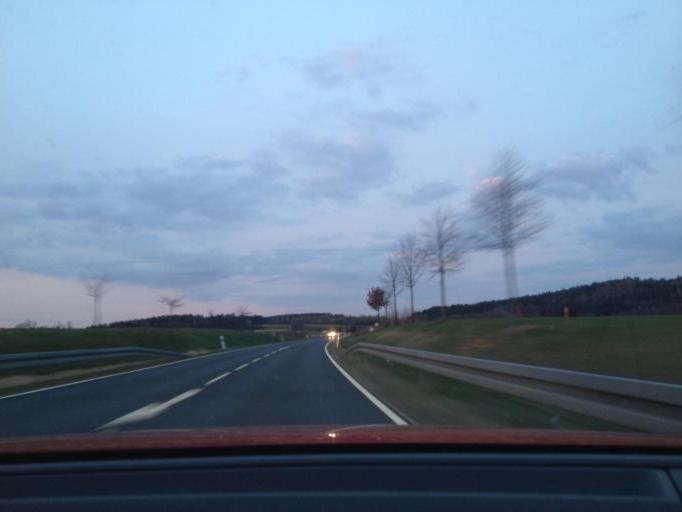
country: DE
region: Bavaria
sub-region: Upper Palatinate
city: Pullenreuth
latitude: 49.9321
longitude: 11.9927
